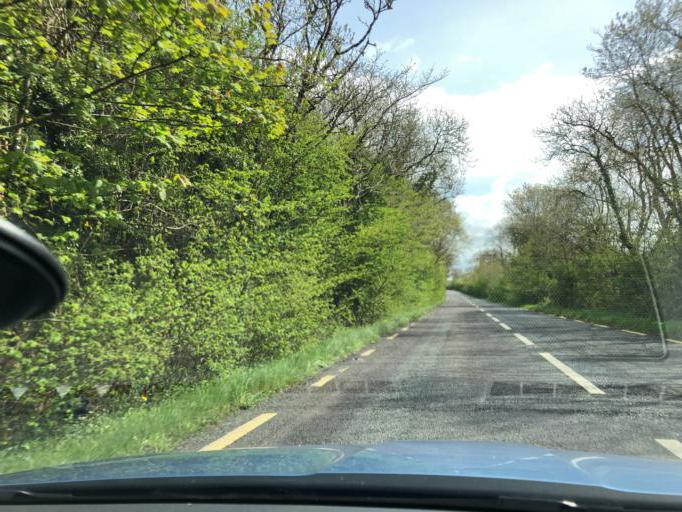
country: IE
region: Munster
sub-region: County Cork
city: Millstreet
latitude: 52.1218
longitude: -9.0635
